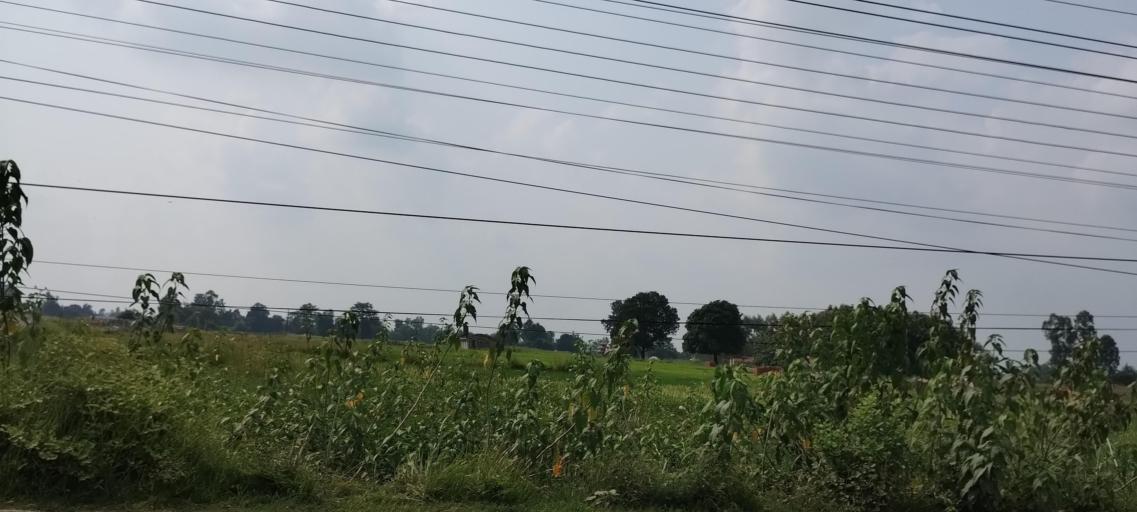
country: NP
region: Mid Western
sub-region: Bheri Zone
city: Nepalgunj
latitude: 28.1648
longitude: 81.6736
